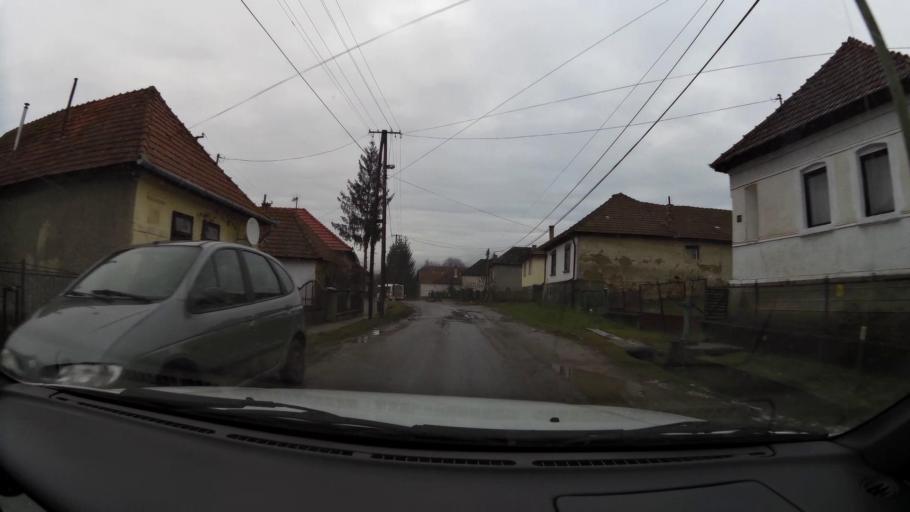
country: HU
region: Borsod-Abauj-Zemplen
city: Rudabanya
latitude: 48.4057
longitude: 20.6406
